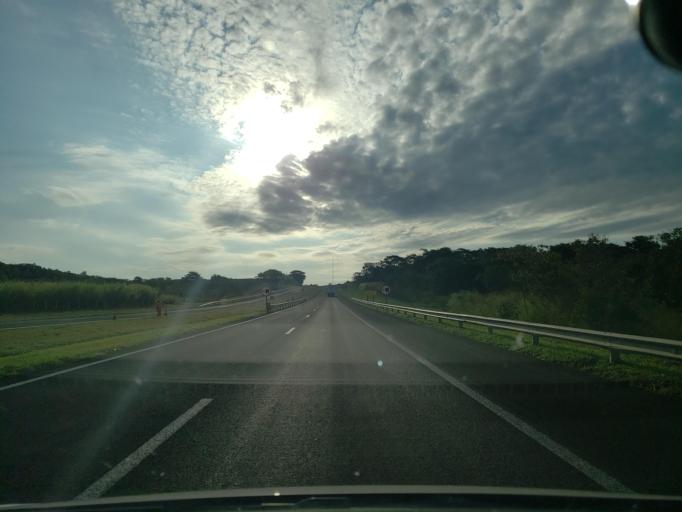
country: BR
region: Sao Paulo
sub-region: Valparaiso
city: Valparaiso
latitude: -21.1618
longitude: -50.9444
